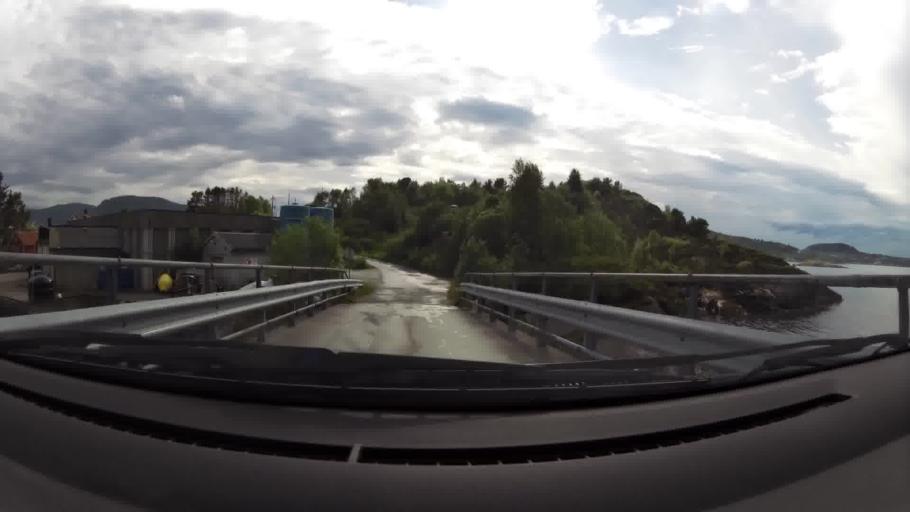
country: NO
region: More og Romsdal
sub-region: Kristiansund
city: Kristiansund
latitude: 63.0615
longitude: 7.7007
